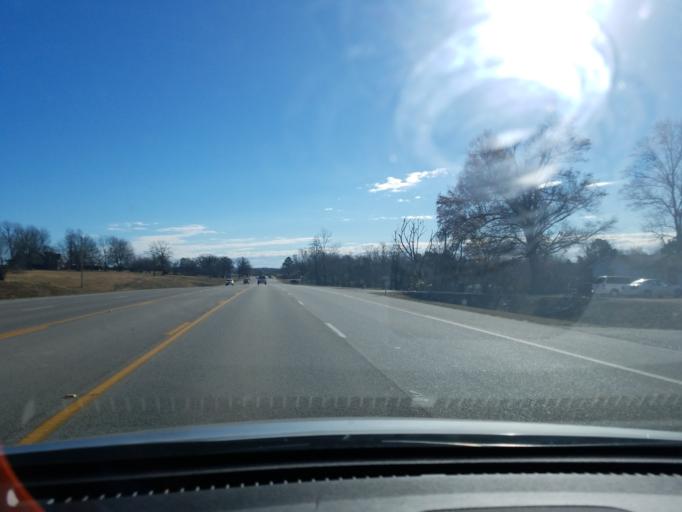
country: US
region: Arkansas
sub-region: Carroll County
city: Berryville
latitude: 36.3860
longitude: -93.6072
